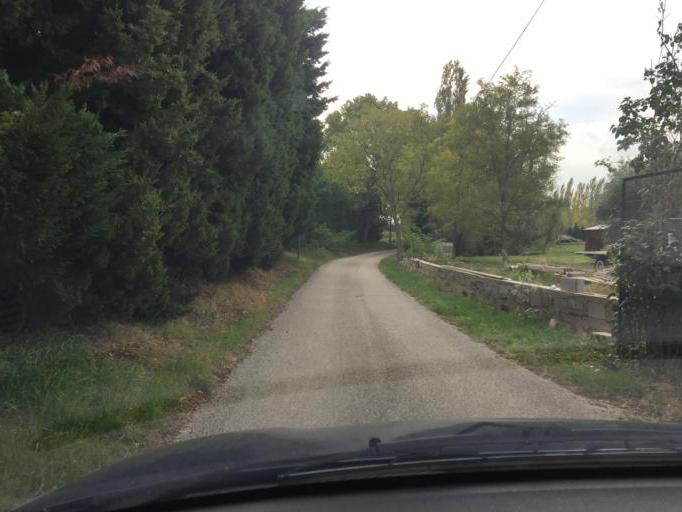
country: FR
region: Provence-Alpes-Cote d'Azur
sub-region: Departement du Vaucluse
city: Camaret-sur-Aigues
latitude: 44.1539
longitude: 4.8673
